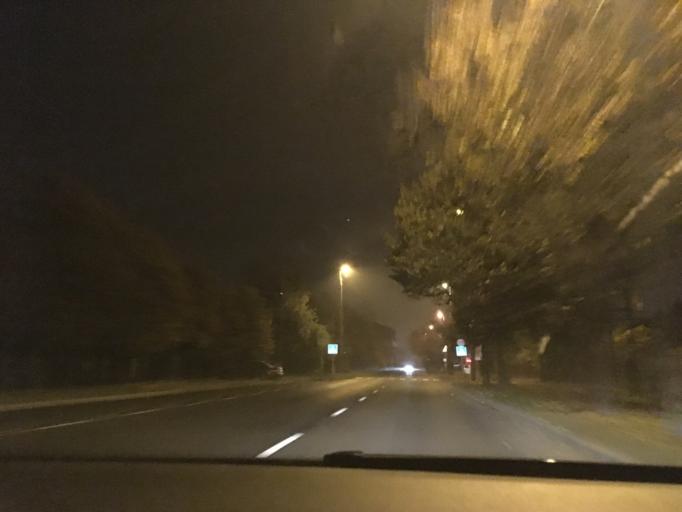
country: HU
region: Hajdu-Bihar
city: Debrecen
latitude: 47.5165
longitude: 21.6086
